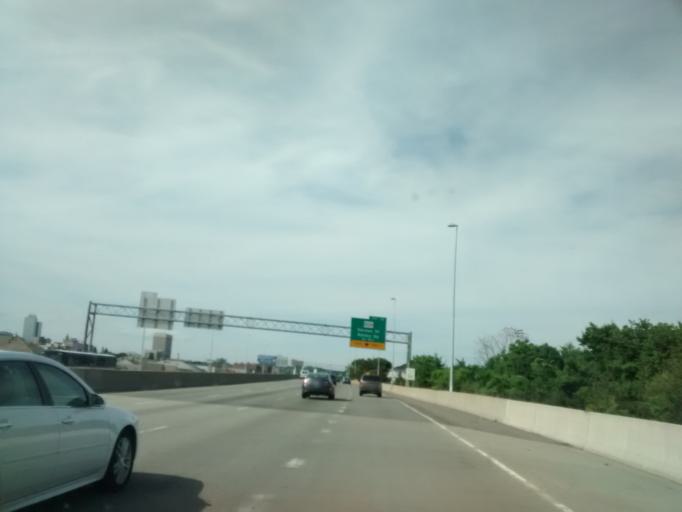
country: US
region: Massachusetts
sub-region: Worcester County
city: Worcester
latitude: 42.2478
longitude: -71.8007
